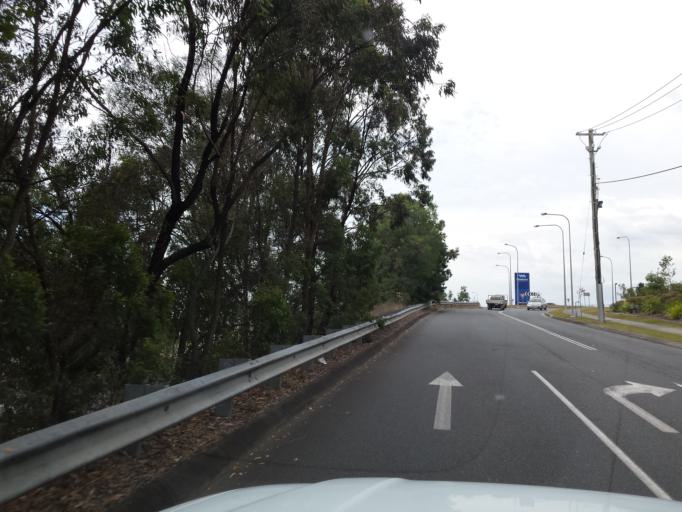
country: AU
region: Queensland
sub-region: Gold Coast
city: Nerang
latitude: -28.0094
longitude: 153.3439
